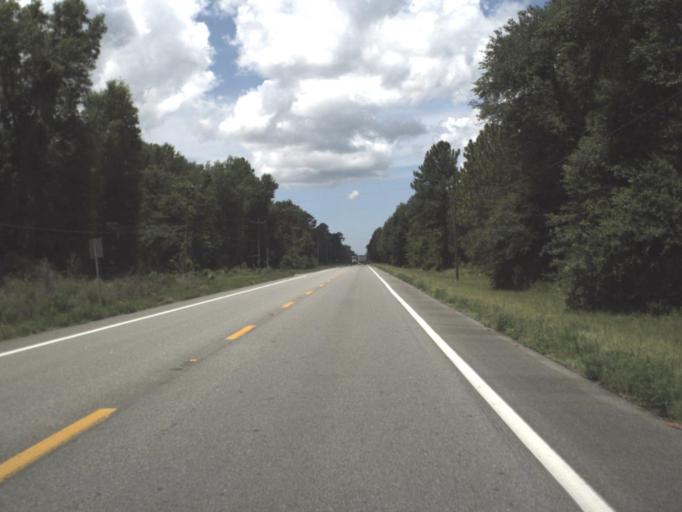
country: US
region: Florida
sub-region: Taylor County
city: Perry
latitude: 30.0990
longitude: -83.6231
